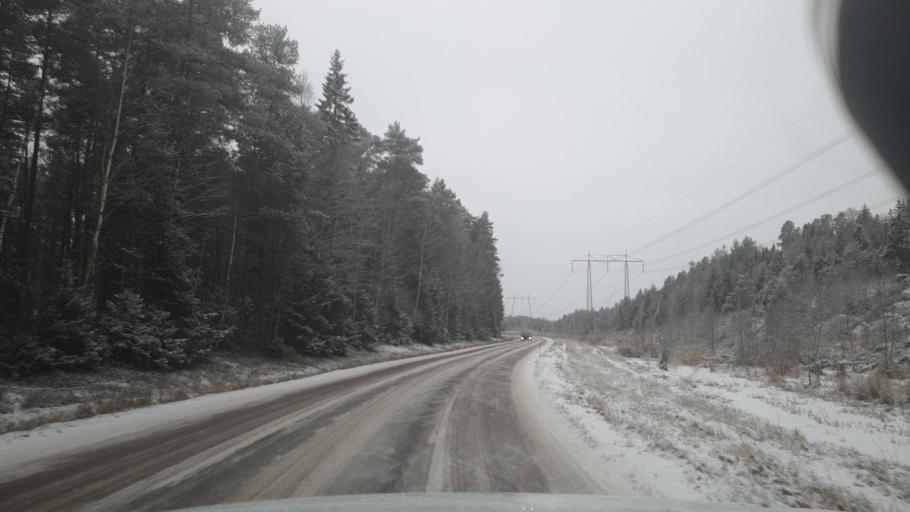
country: SE
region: Vaermland
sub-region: Grums Kommun
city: Grums
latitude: 59.4360
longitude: 12.9796
